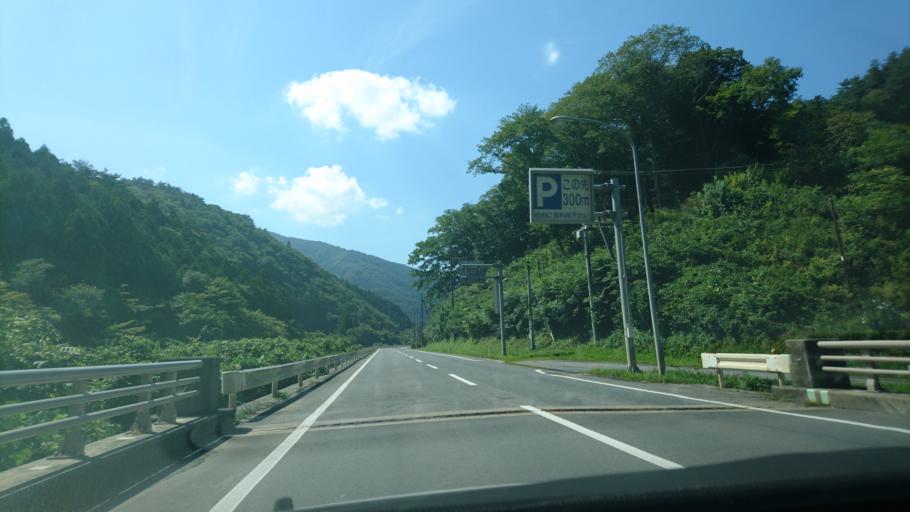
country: JP
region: Iwate
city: Ofunato
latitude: 39.0223
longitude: 141.5441
